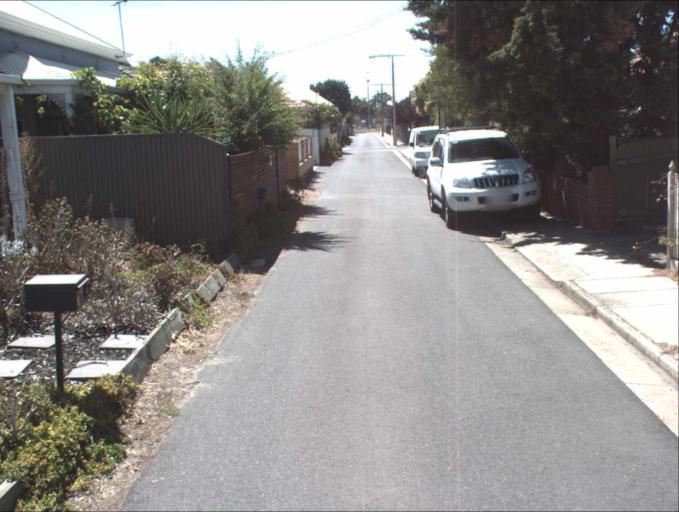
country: AU
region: South Australia
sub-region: Port Adelaide Enfield
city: Birkenhead
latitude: -34.8342
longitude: 138.4889
